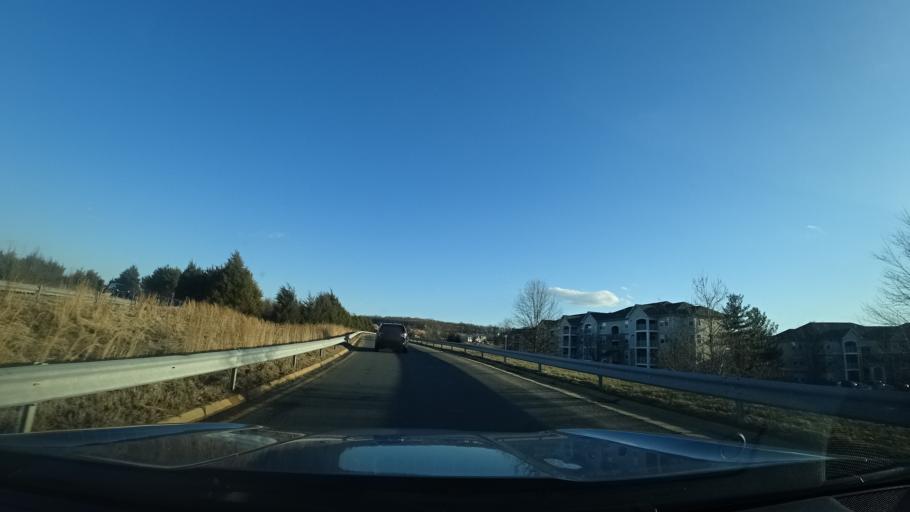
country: US
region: Virginia
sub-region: Loudoun County
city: Dulles Town Center
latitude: 39.0296
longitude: -77.4034
